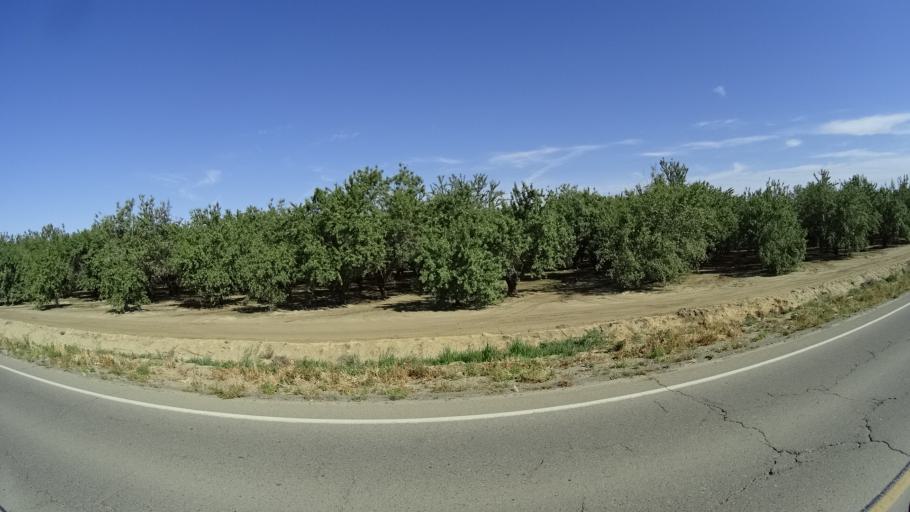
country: US
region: California
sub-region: Kings County
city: Avenal
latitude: 36.0965
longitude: -120.0639
